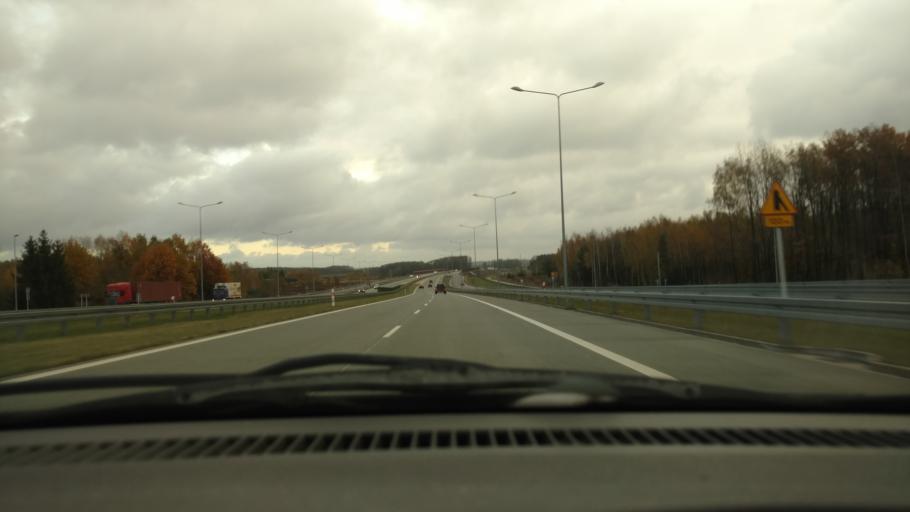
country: PL
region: Lodz Voivodeship
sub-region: Powiat lodzki wschodni
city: Rzgow
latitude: 51.6389
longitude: 19.5017
